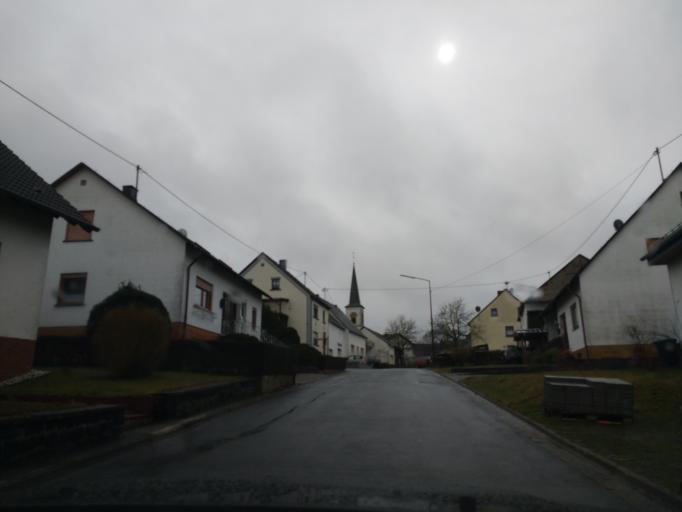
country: DE
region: Rheinland-Pfalz
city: Rascheid
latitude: 49.7142
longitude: 6.9355
